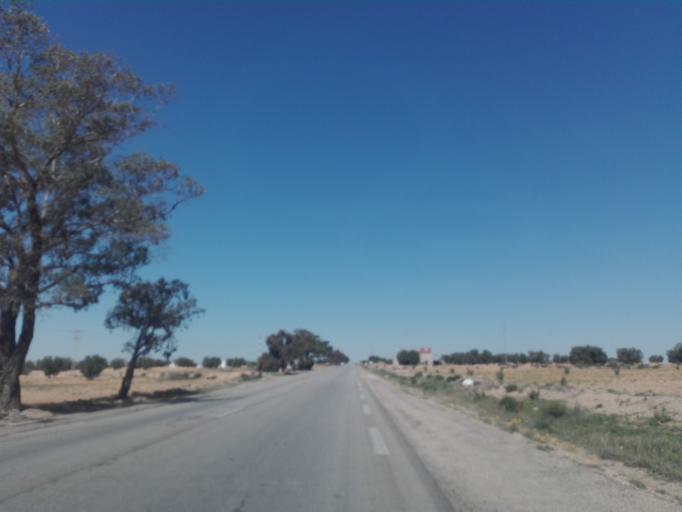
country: TN
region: Safaqis
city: Bi'r `Ali Bin Khalifah
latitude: 34.7526
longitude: 10.3406
